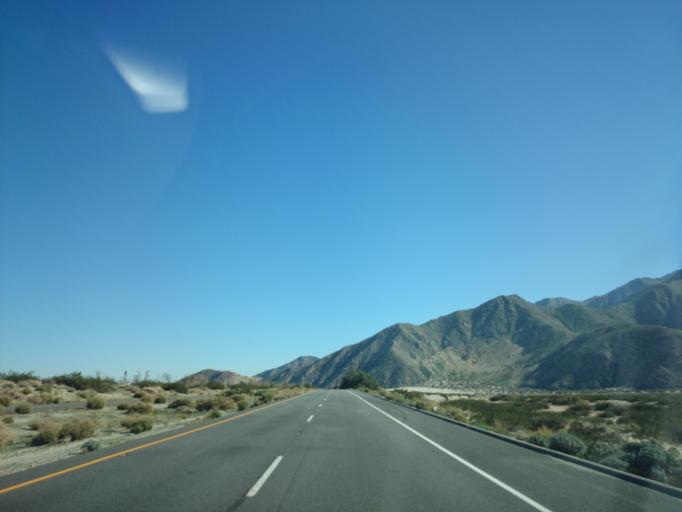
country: US
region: California
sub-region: Riverside County
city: Garnet
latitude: 33.9104
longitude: -116.6570
